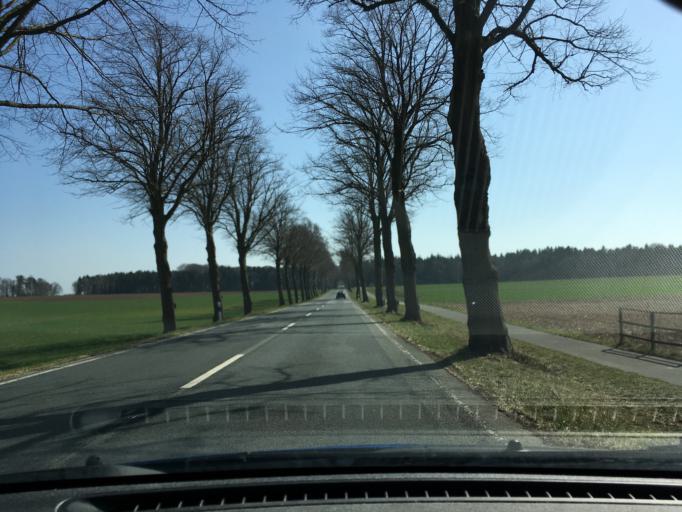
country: DE
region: Lower Saxony
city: Wriedel
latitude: 53.0659
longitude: 10.2856
